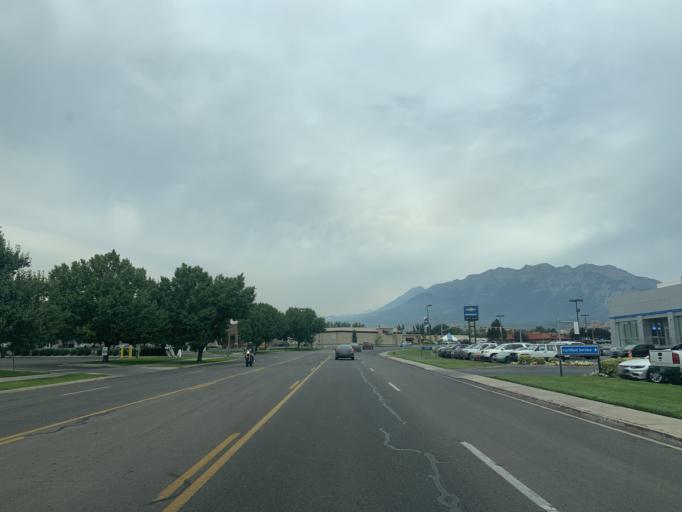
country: US
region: Utah
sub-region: Utah County
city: Provo
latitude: 40.2612
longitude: -111.6679
